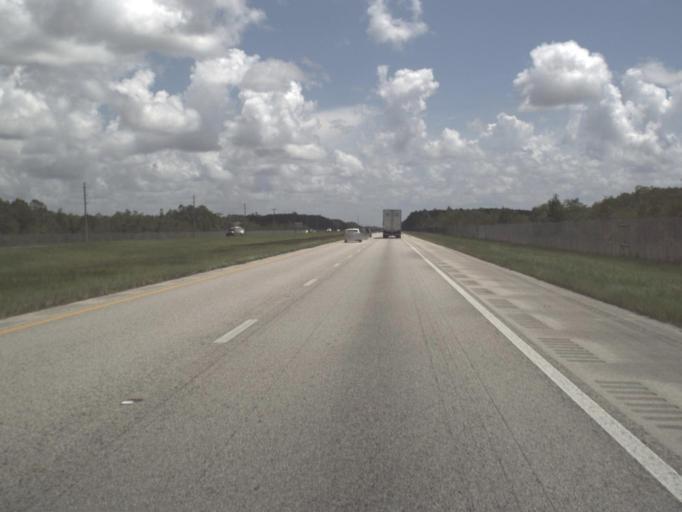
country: US
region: Florida
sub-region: Collier County
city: Immokalee
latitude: 26.1671
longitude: -81.1793
